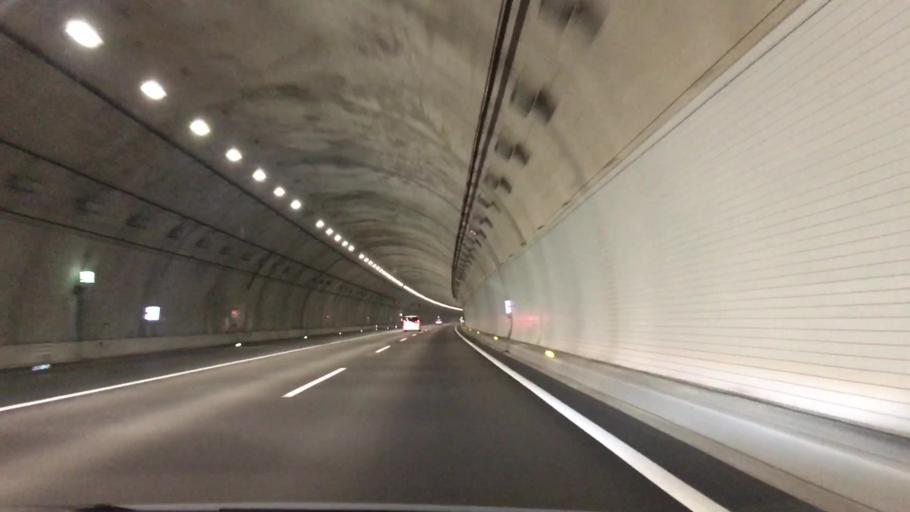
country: JP
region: Shizuoka
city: Hamakita
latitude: 34.8681
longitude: 137.6748
